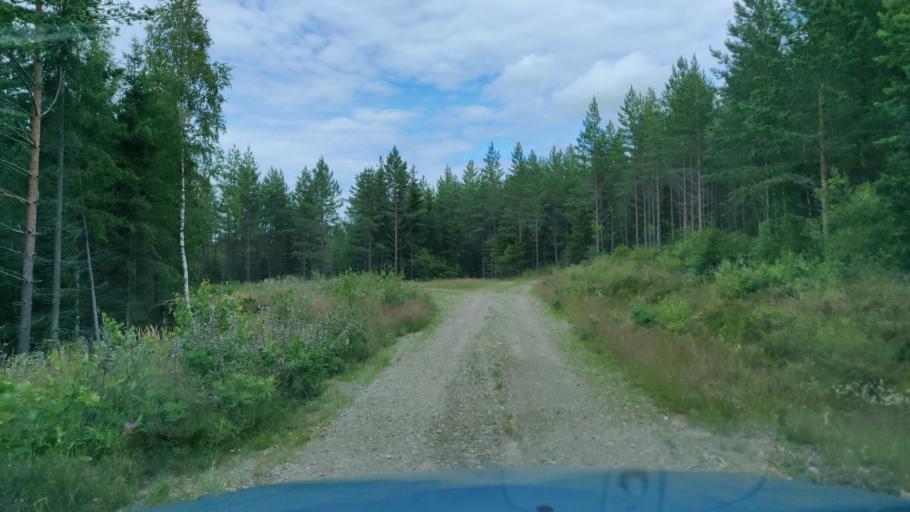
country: SE
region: Vaermland
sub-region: Hagfors Kommun
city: Hagfors
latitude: 59.9697
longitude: 13.5825
